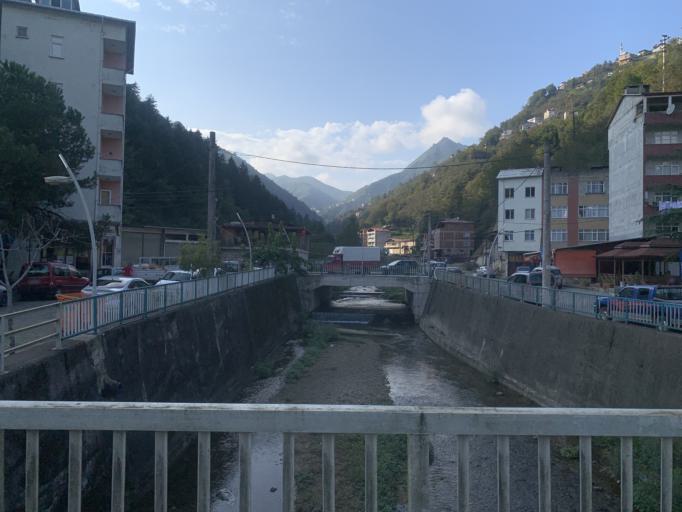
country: TR
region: Trabzon
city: Dernekpazari
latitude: 40.8318
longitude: 40.2696
